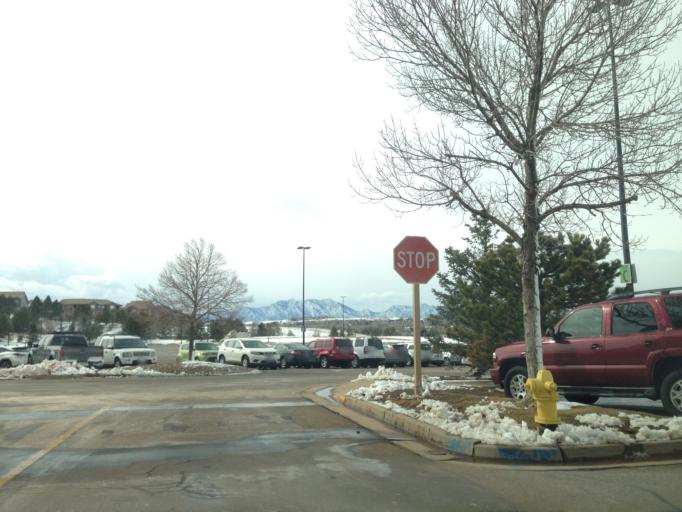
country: US
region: Colorado
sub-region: Boulder County
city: Superior
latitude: 39.9351
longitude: -105.1342
